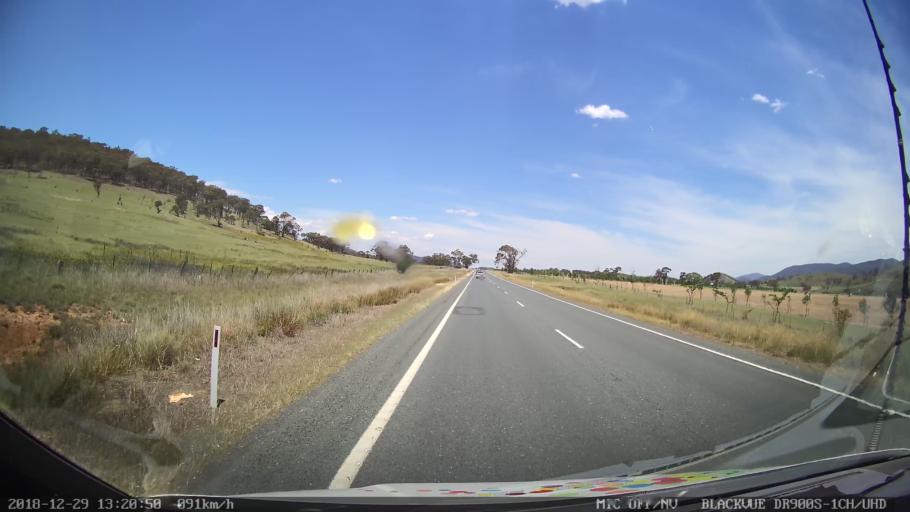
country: AU
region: Australian Capital Territory
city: Macarthur
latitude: -35.7841
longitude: 149.1624
